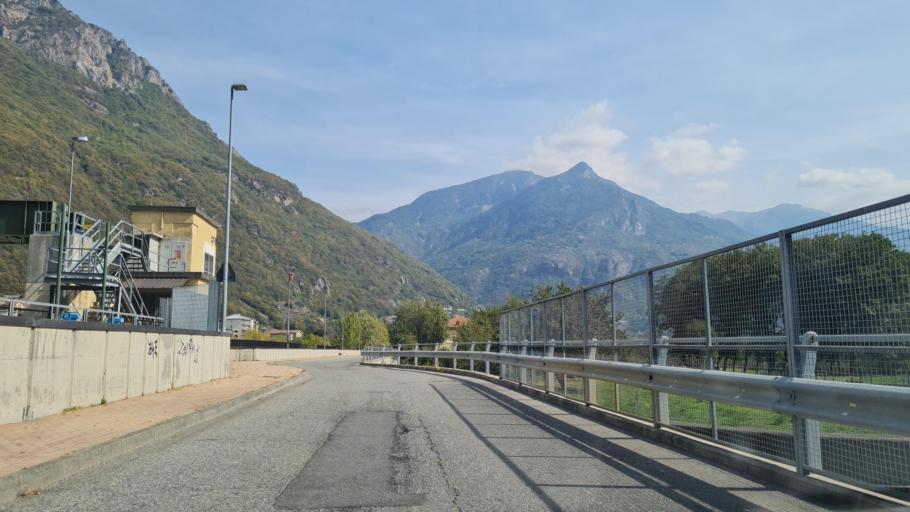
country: IT
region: Aosta Valley
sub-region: Valle d'Aosta
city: Donnas
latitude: 45.6014
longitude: 7.7624
